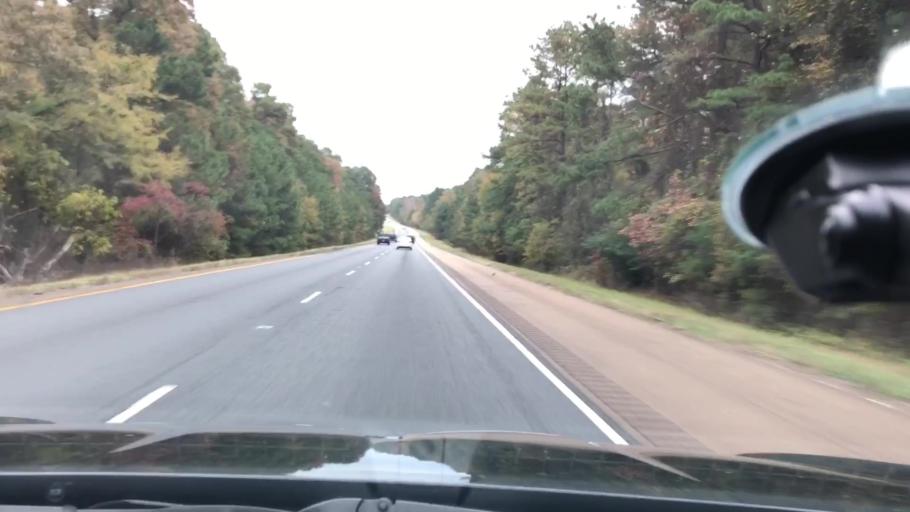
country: US
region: Arkansas
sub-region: Clark County
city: Gurdon
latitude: 33.9415
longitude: -93.2443
